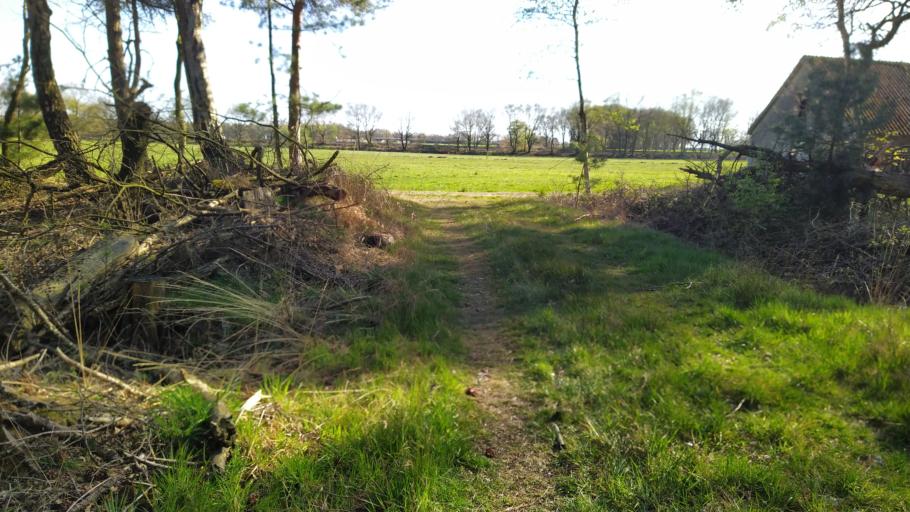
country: DE
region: Lower Saxony
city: Gross Meckelsen
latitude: 53.2903
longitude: 9.4773
